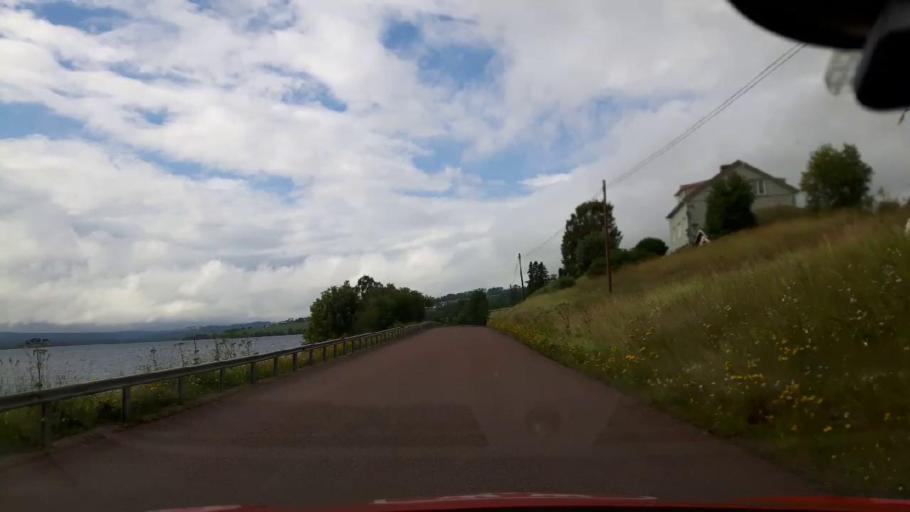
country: SE
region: Jaemtland
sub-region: Krokoms Kommun
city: Valla
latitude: 63.3835
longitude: 13.9892
